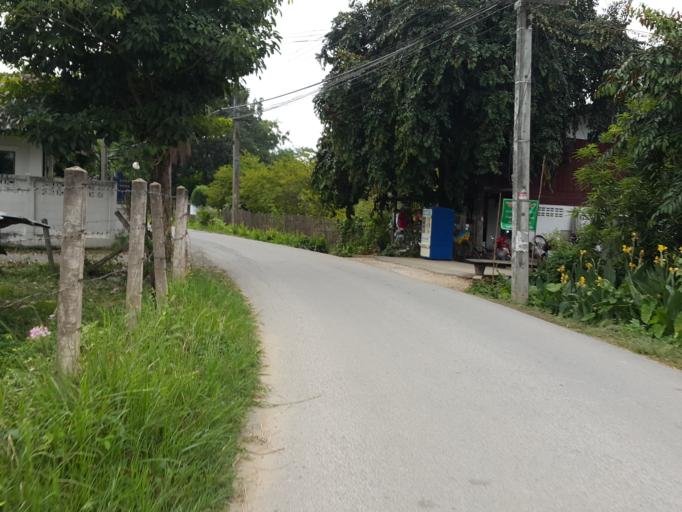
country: TH
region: Chiang Mai
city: San Kamphaeng
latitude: 18.7815
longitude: 99.0994
